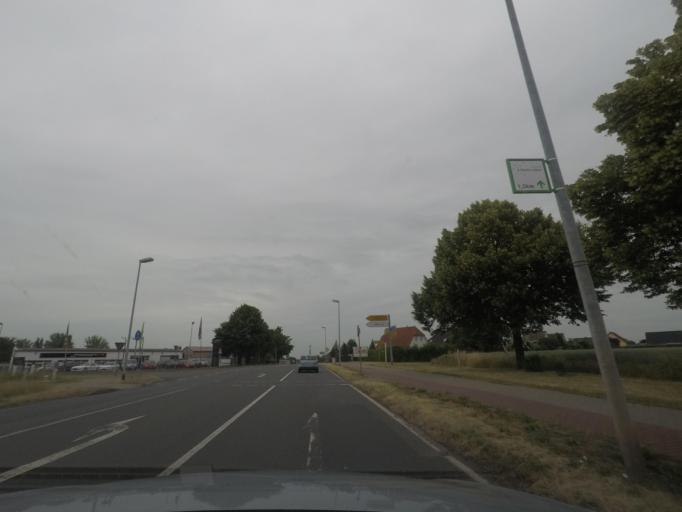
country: DE
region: Saxony-Anhalt
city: Oschersleben
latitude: 52.0382
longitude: 11.2482
